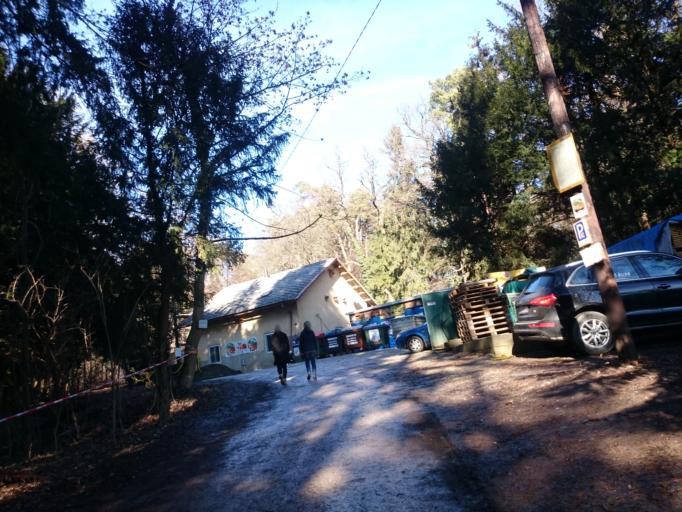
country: AT
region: Styria
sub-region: Graz Stadt
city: Graz
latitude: 47.0831
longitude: 15.4642
